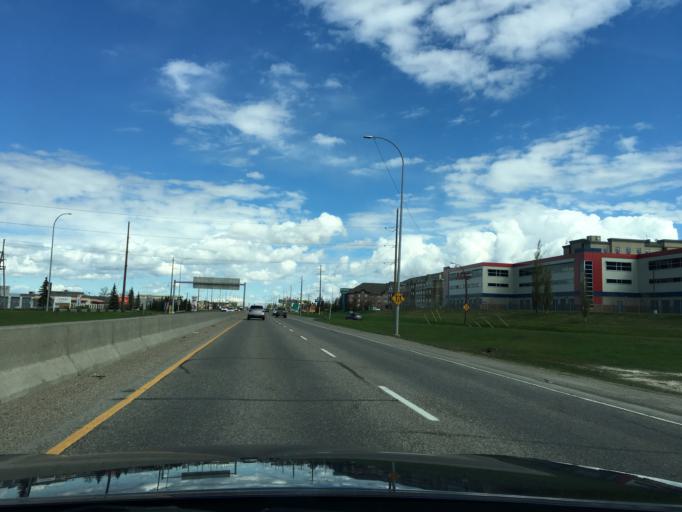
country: CA
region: Alberta
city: Calgary
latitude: 51.0692
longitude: -114.0017
